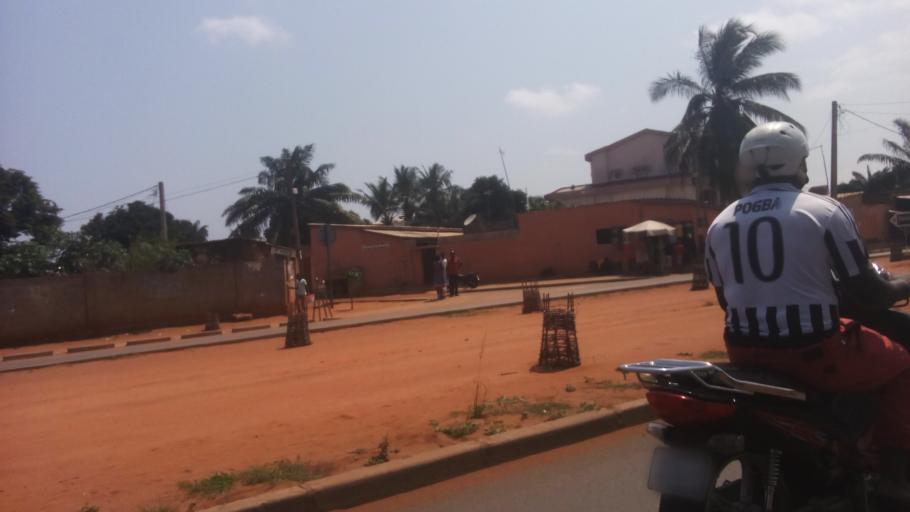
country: TG
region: Maritime
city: Lome
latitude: 6.1906
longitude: 1.2499
